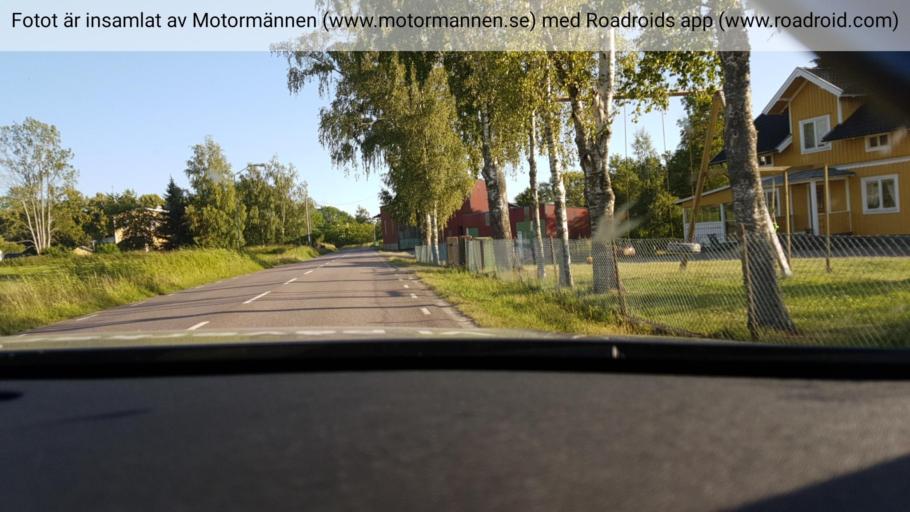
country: SE
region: Vaestra Goetaland
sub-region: Toreboda Kommun
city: Toereboda
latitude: 58.5809
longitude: 14.0046
